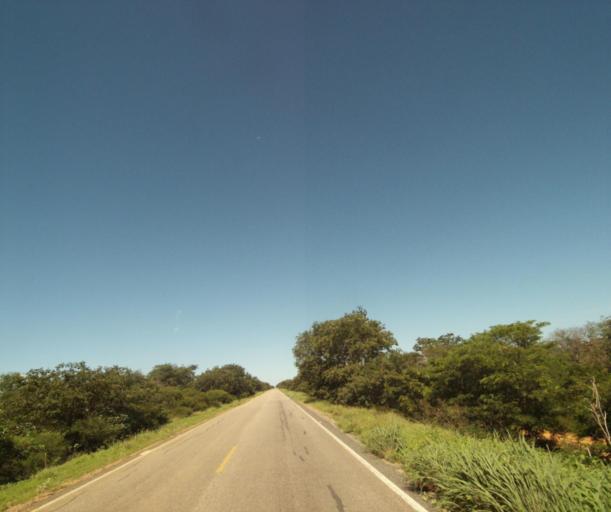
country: BR
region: Bahia
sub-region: Palmas De Monte Alto
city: Palmas de Monte Alto
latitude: -14.2615
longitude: -43.3099
